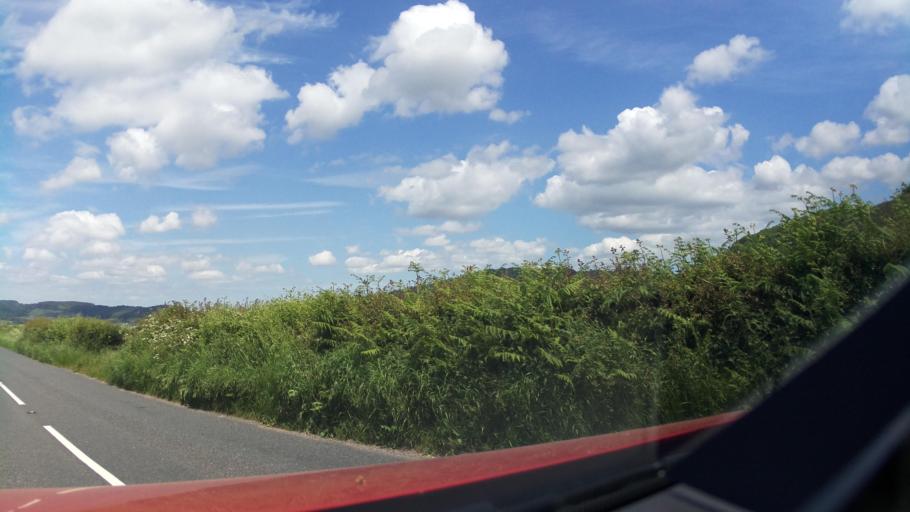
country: GB
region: Wales
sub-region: Monmouthshire
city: Monmouth
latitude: 51.7916
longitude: -2.7162
